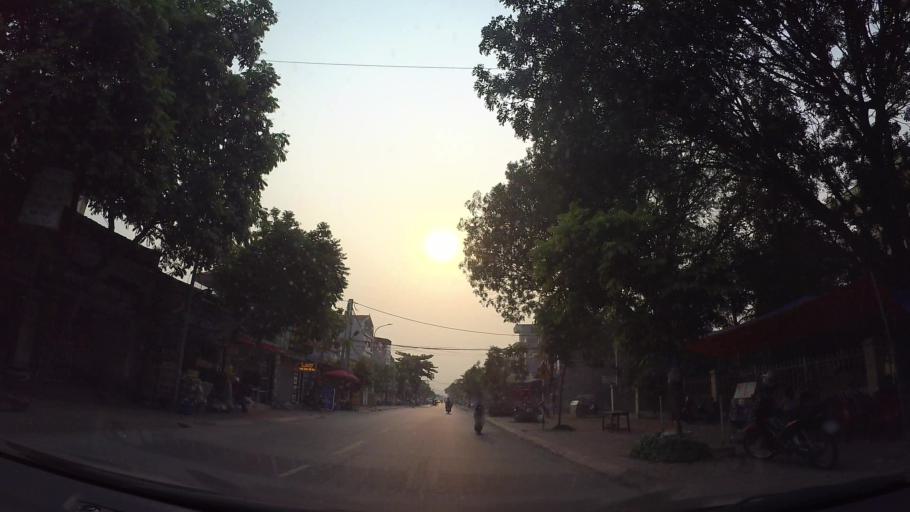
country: VN
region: Ha Noi
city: Thuong Tin
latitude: 20.8686
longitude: 105.8429
